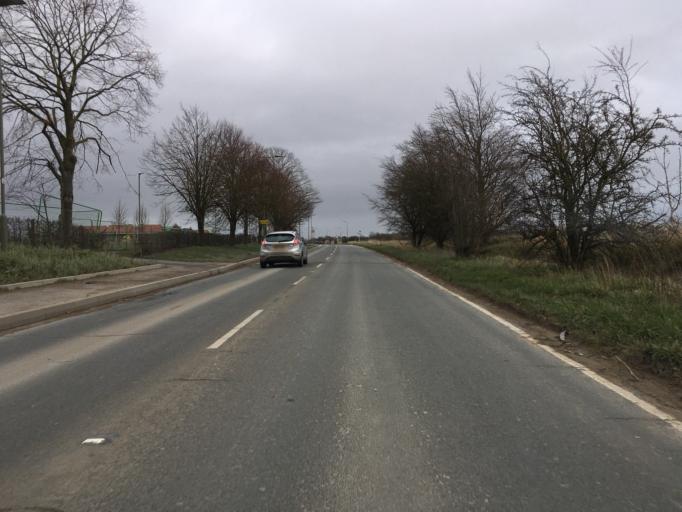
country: GB
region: England
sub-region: Oxfordshire
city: Wantage
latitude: 51.5919
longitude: -1.4046
